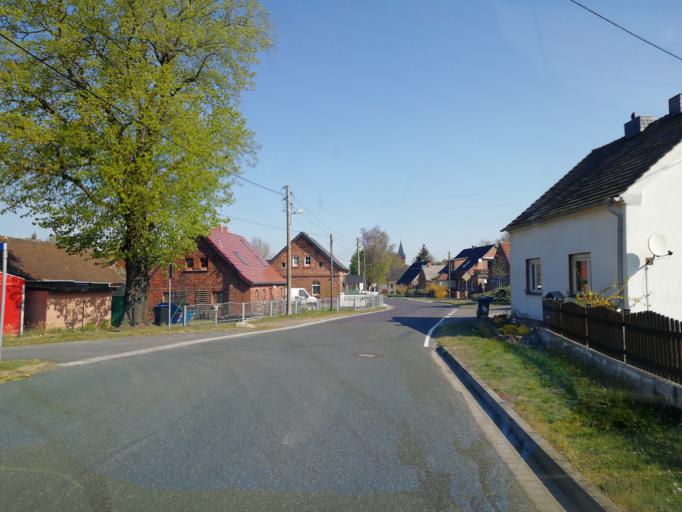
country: DE
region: Brandenburg
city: Bronkow
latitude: 51.6997
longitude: 13.8744
